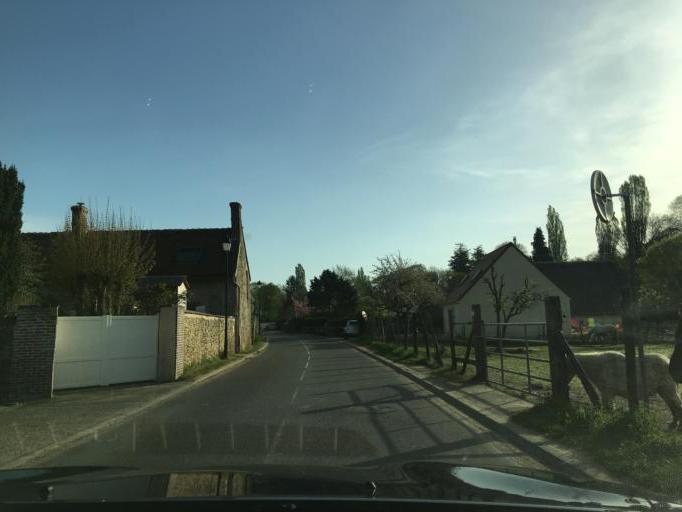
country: FR
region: Centre
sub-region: Departement d'Eure-et-Loir
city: Epernon
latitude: 48.6187
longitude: 1.6754
